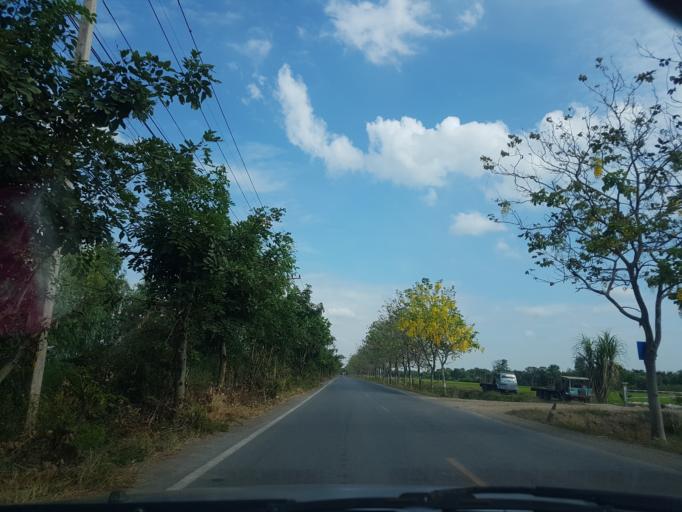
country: TH
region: Pathum Thani
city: Nong Suea
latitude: 14.1356
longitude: 100.8832
